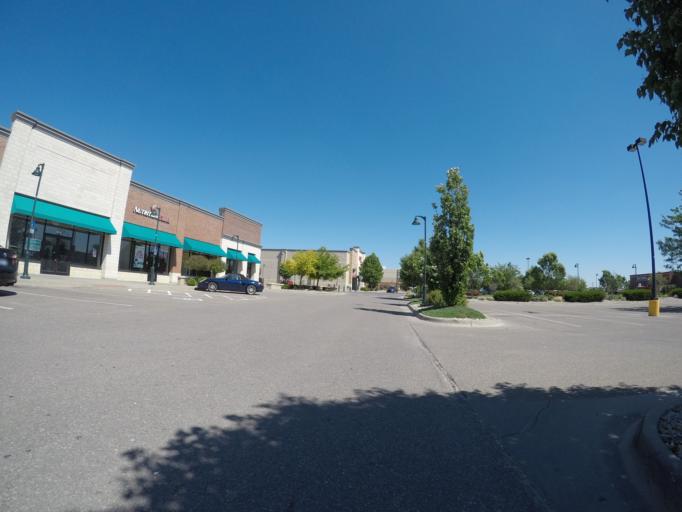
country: US
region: Kansas
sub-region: Riley County
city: Manhattan
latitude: 39.1836
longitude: -96.5602
